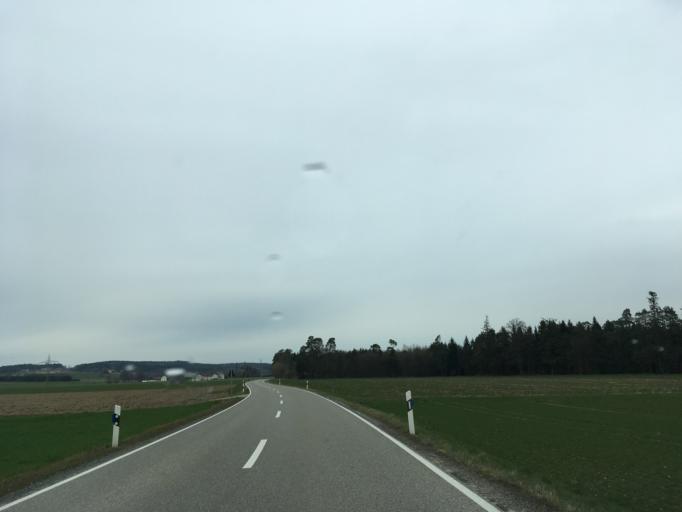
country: DE
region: Bavaria
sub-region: Upper Bavaria
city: Schnaitsee
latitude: 48.0875
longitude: 12.4094
